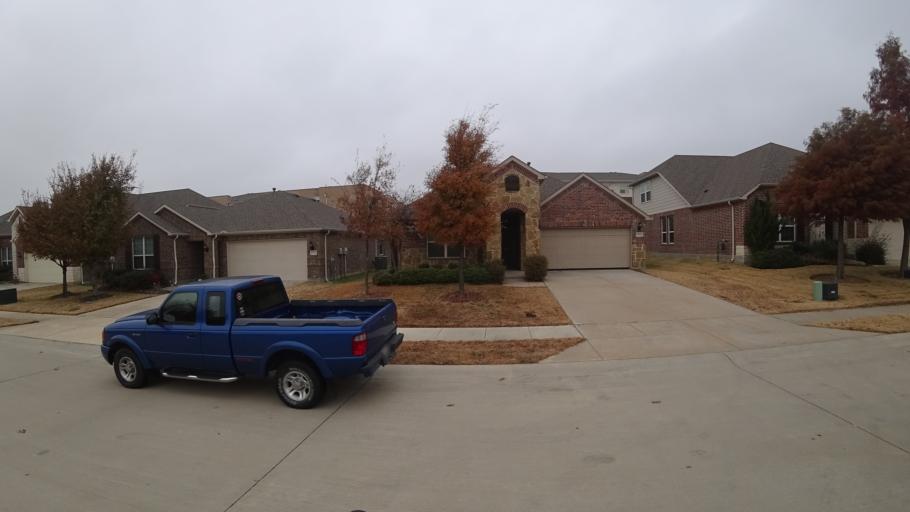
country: US
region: Texas
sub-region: Denton County
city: The Colony
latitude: 33.0623
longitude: -96.9091
